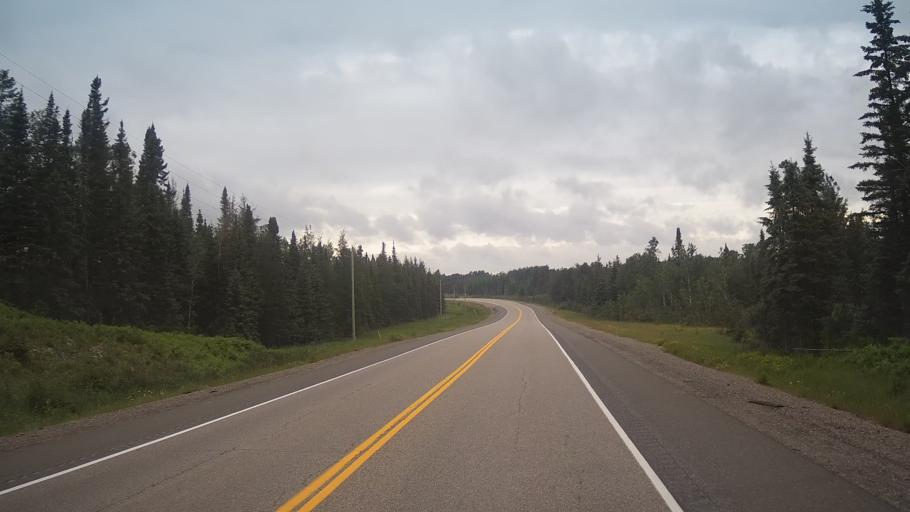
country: CA
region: Ontario
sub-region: Thunder Bay District
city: Thunder Bay
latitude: 48.8396
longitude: -89.9395
